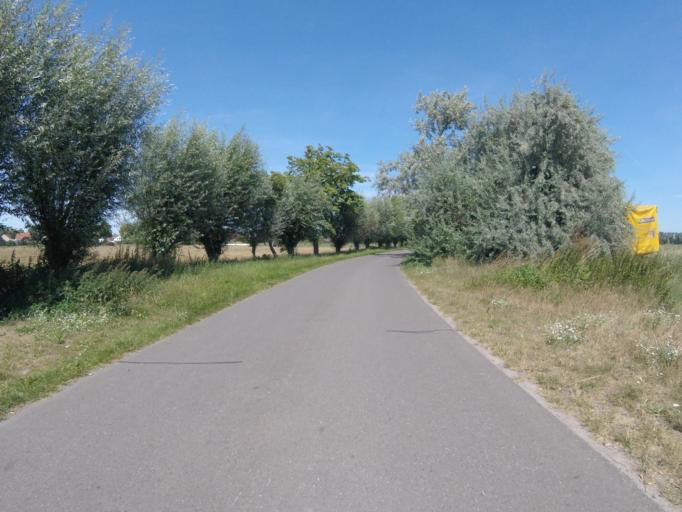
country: DE
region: Brandenburg
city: Mittenwalde
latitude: 52.2815
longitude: 13.5436
